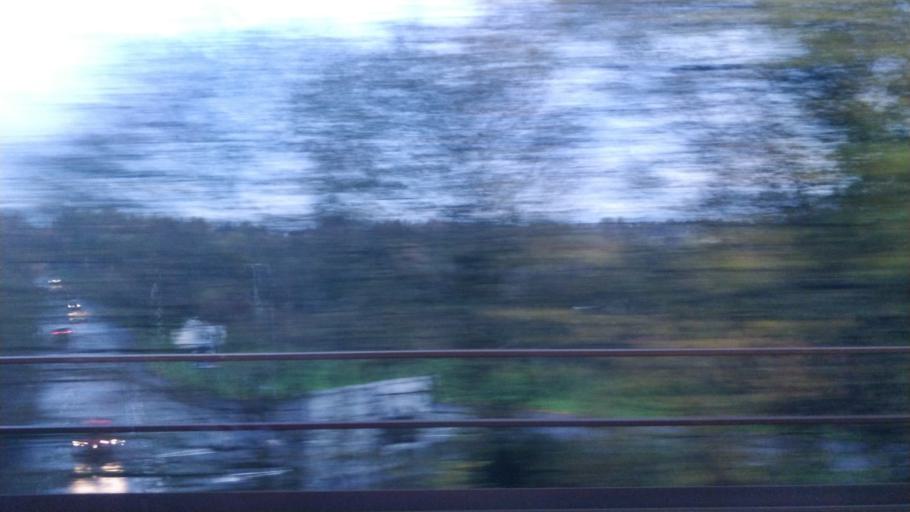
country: GB
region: England
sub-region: Borough of Wigan
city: Hindley
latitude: 53.5386
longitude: -2.5930
